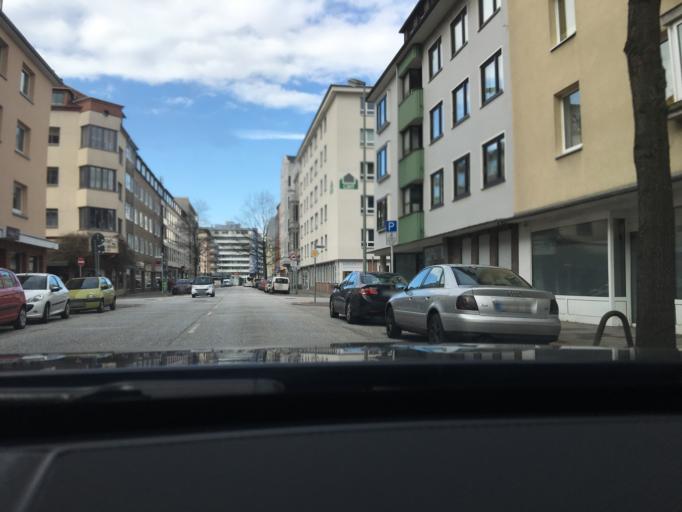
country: DE
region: Bremen
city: Bremerhaven
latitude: 53.5483
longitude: 8.5745
